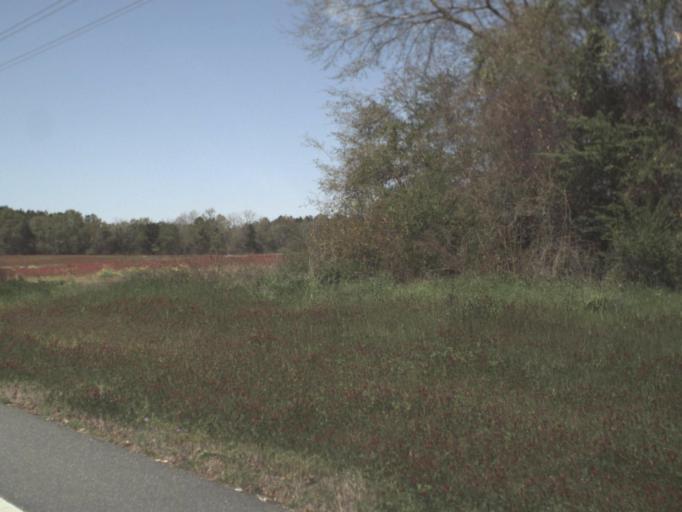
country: US
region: Florida
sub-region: Jackson County
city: Graceville
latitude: 30.9727
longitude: -85.6273
